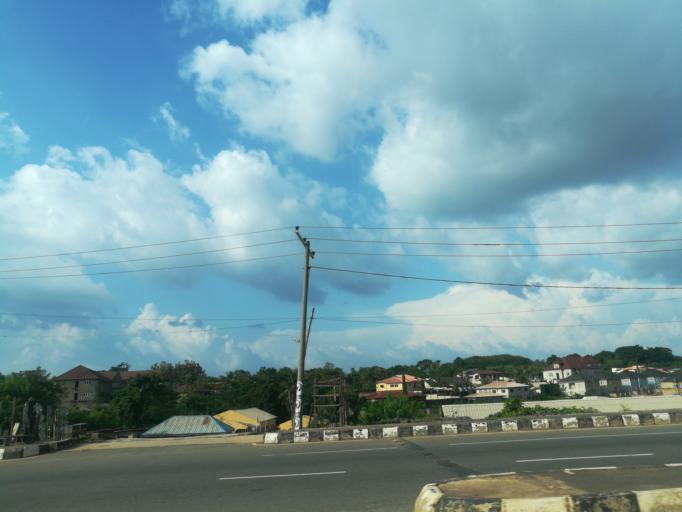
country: NG
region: Oyo
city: Ibadan
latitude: 7.4002
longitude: 3.8743
